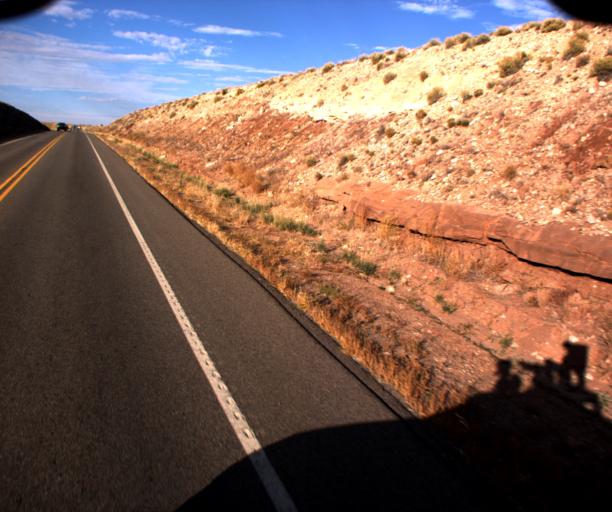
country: US
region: New Mexico
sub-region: San Juan County
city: Shiprock
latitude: 36.9284
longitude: -109.1626
